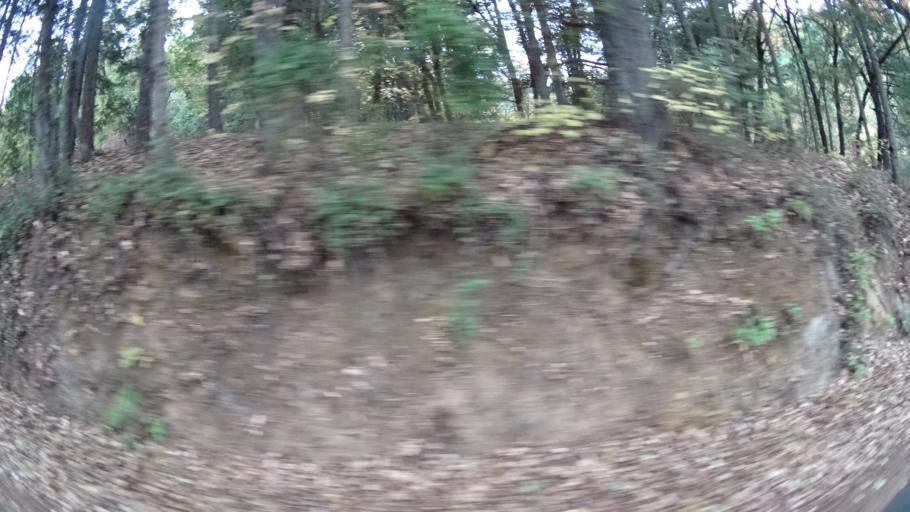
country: US
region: California
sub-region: Siskiyou County
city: Happy Camp
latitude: 41.8065
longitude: -123.3689
